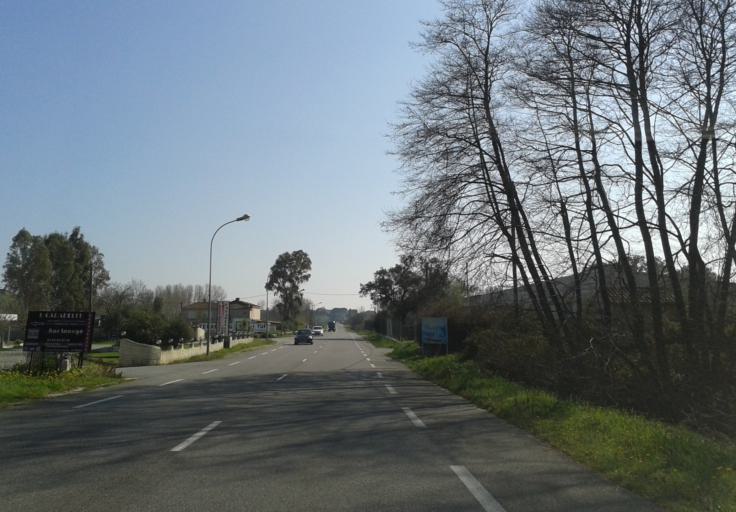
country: FR
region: Corsica
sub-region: Departement de la Haute-Corse
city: Linguizzetta
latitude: 42.2097
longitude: 9.5341
